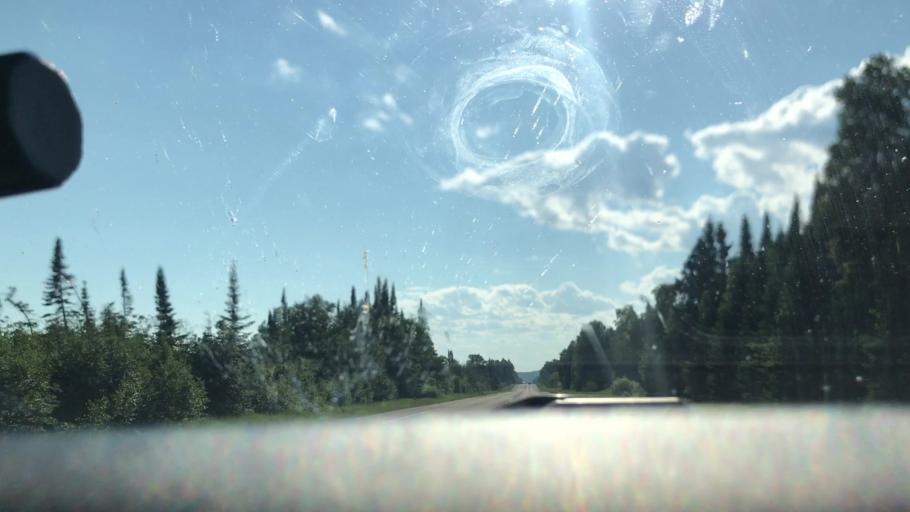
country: US
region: Minnesota
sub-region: Cook County
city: Grand Marais
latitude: 47.7971
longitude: -90.1160
